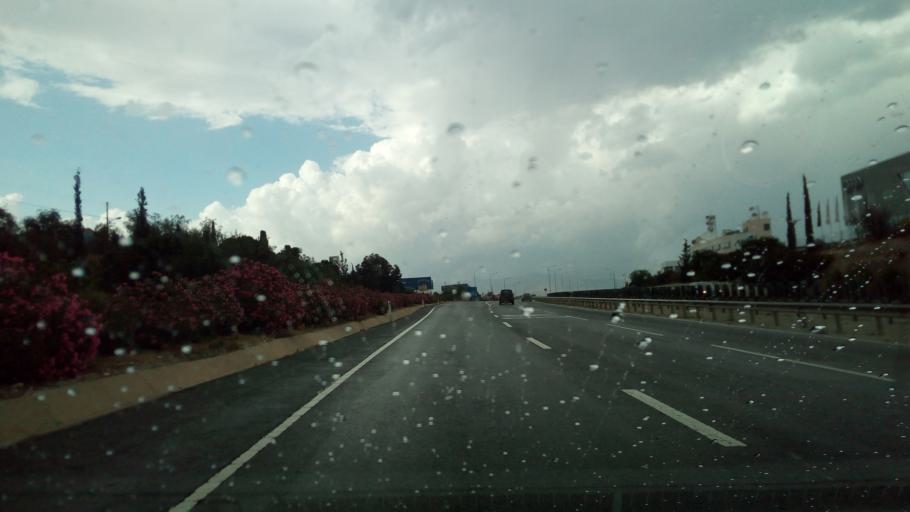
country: CY
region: Lefkosia
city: Nicosia
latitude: 35.1234
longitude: 33.3628
